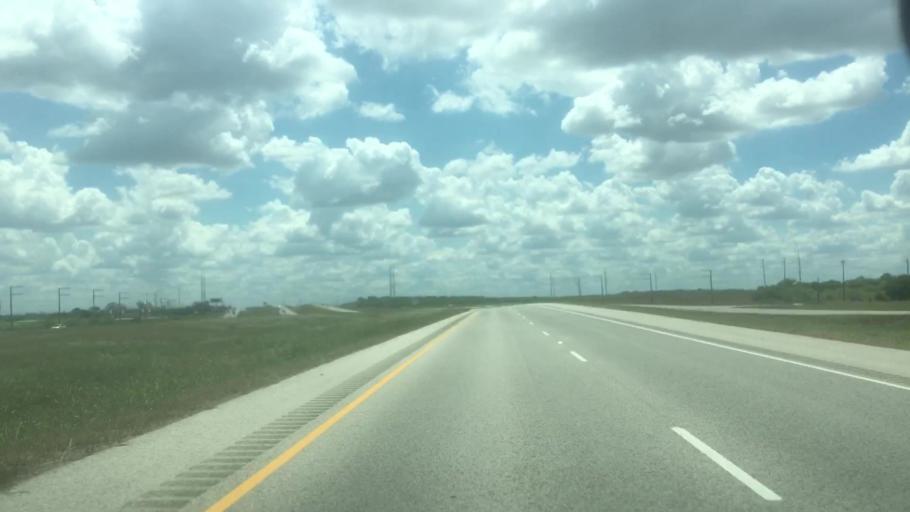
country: US
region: Texas
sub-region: Caldwell County
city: Uhland
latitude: 30.0178
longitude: -97.6880
